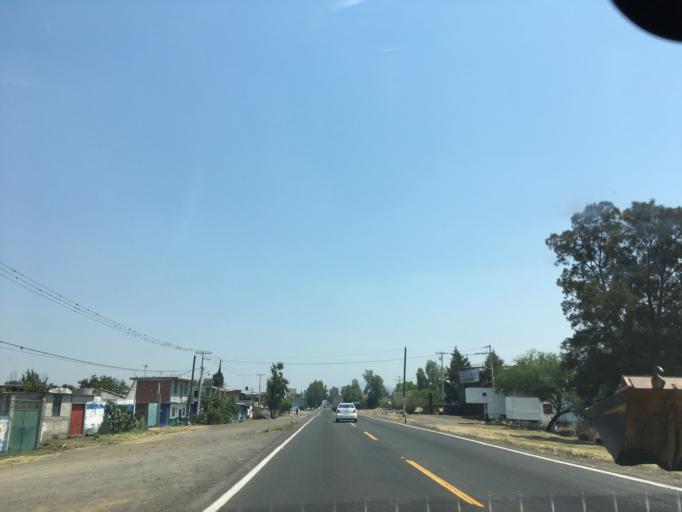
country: MX
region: Michoacan
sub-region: Cuitzeo
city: Cuamio
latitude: 20.0310
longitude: -101.1528
